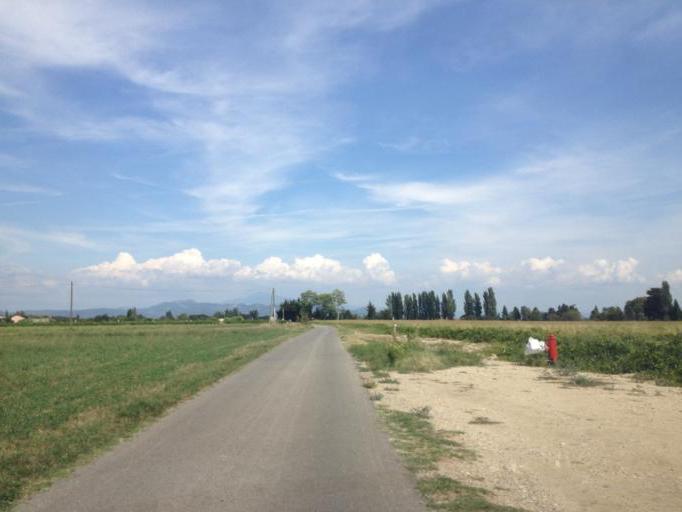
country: FR
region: Provence-Alpes-Cote d'Azur
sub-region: Departement du Vaucluse
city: Camaret-sur-Aigues
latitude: 44.1514
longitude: 4.8489
